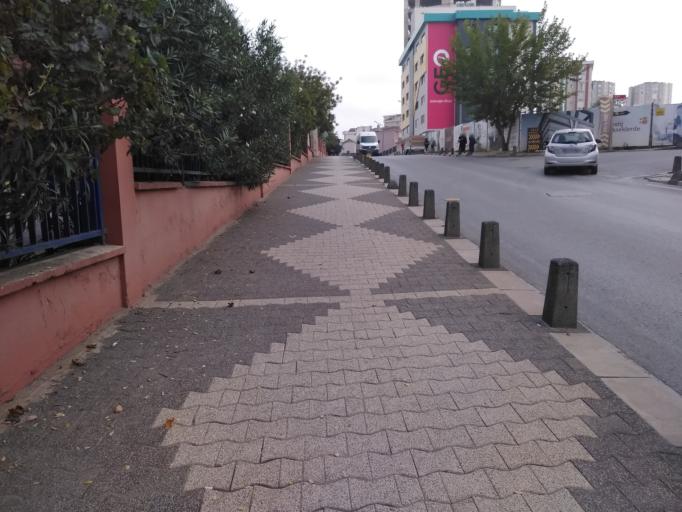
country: TR
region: Istanbul
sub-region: Atasehir
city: Atasehir
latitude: 40.9821
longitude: 29.1080
